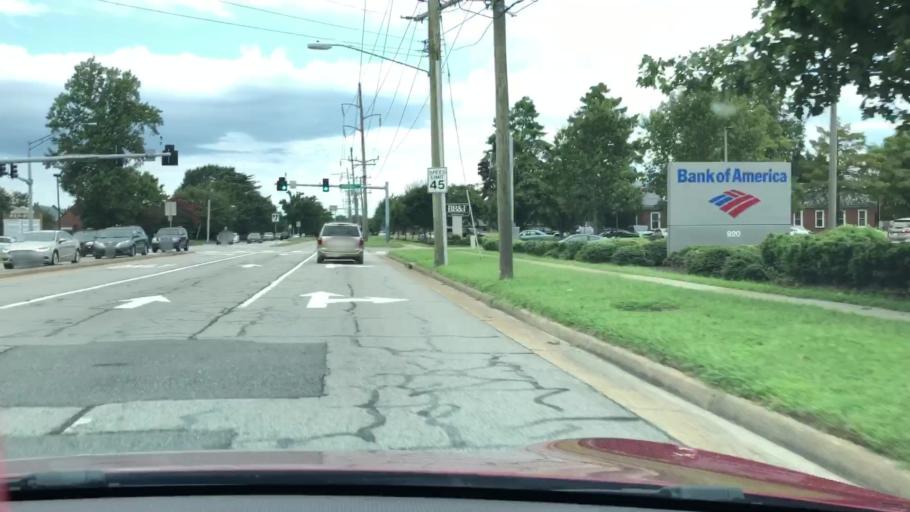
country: US
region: Virginia
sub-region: City of Virginia Beach
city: Virginia Beach
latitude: 36.8567
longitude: -76.0255
